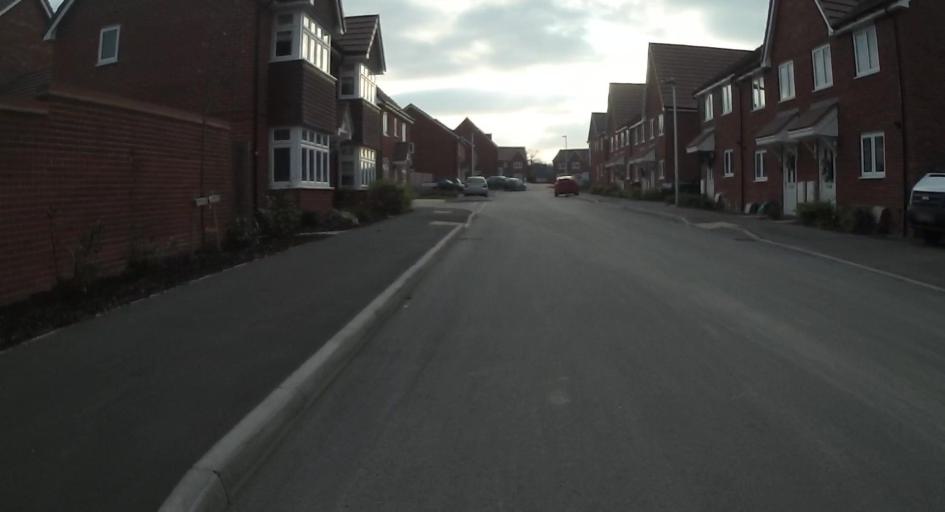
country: GB
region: England
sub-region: Wokingham
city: Wokingham
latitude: 51.4229
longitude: -0.8416
